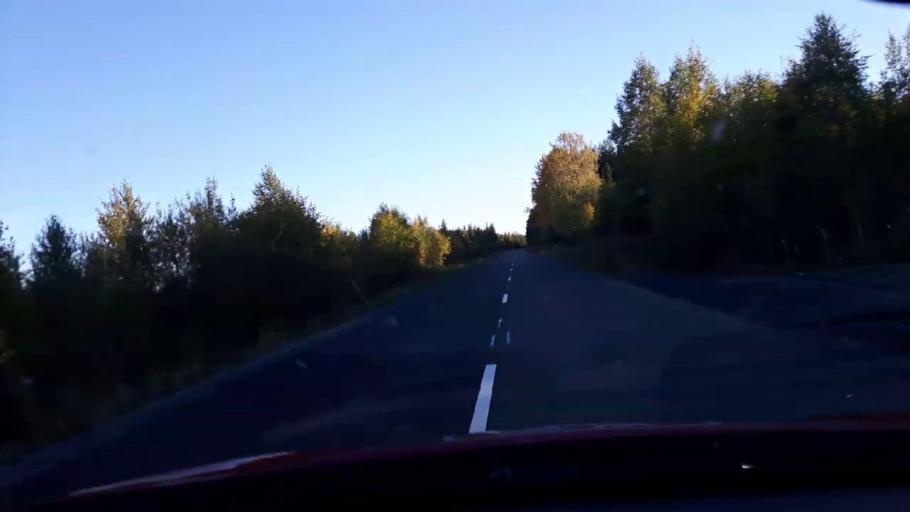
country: SE
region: Jaemtland
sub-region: OEstersunds Kommun
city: Lit
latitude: 63.4754
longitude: 14.8792
